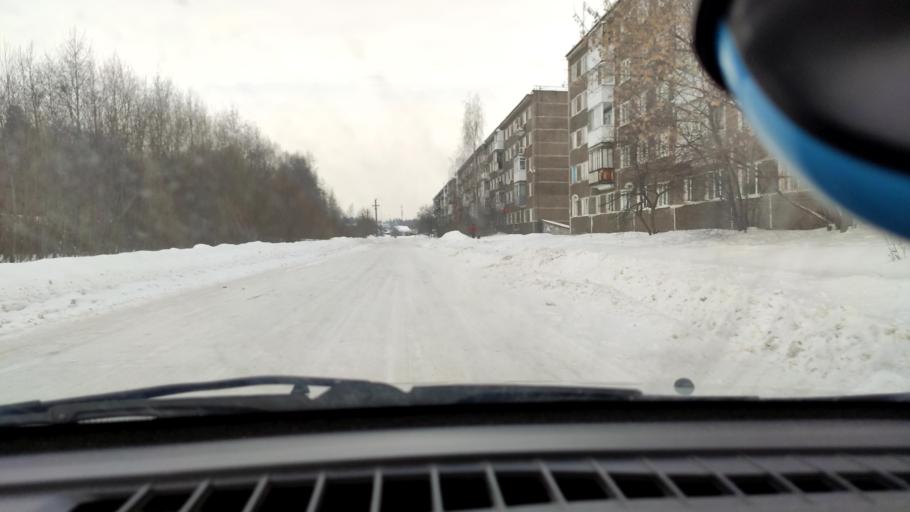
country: RU
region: Perm
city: Overyata
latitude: 58.0771
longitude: 55.8702
